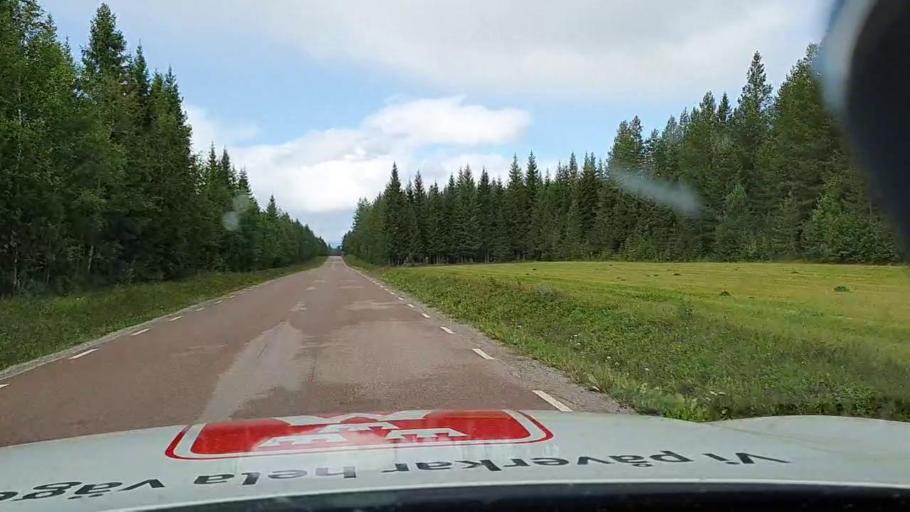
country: SE
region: Jaemtland
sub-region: Stroemsunds Kommun
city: Stroemsund
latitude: 63.8713
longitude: 15.3687
